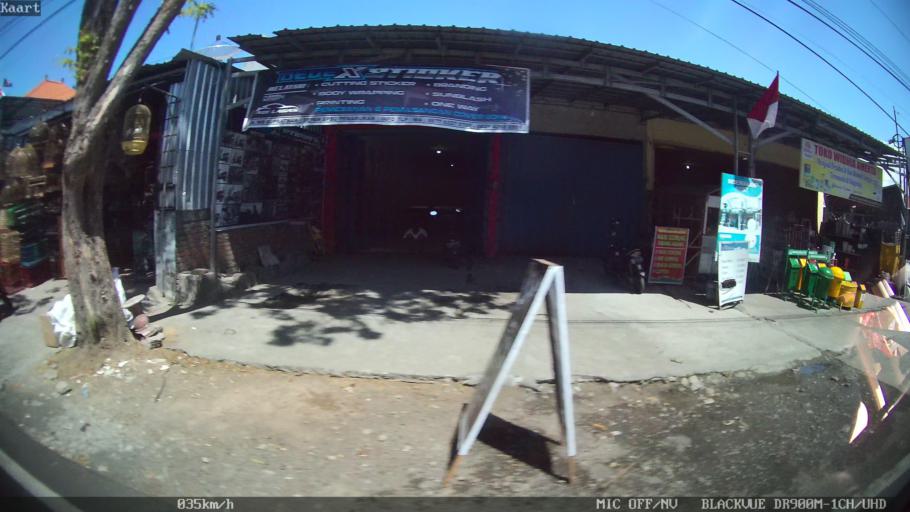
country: ID
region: Bali
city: Banjar Sidayu
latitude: -8.0954
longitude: 115.1119
